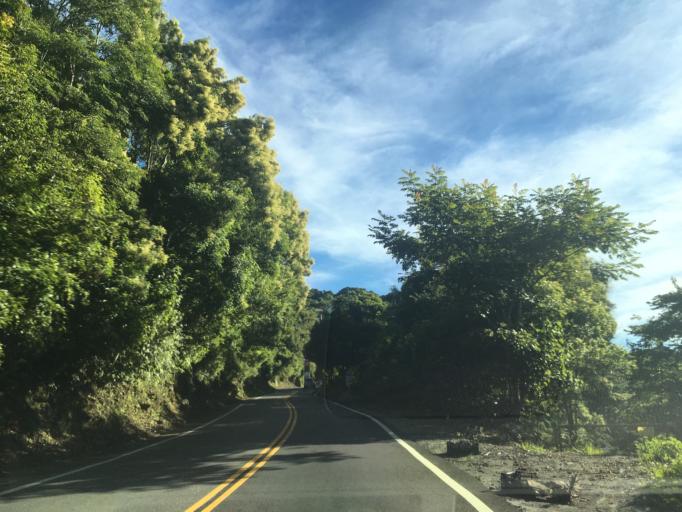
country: TW
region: Taiwan
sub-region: Nantou
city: Puli
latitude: 24.0343
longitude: 121.1546
